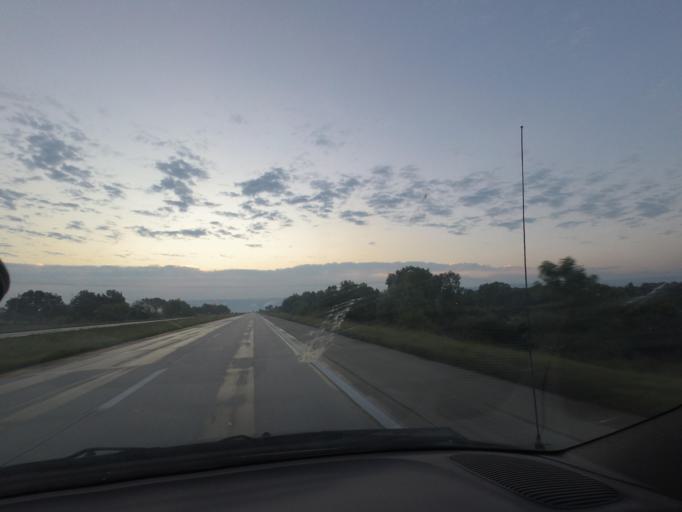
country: US
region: Missouri
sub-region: Macon County
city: Macon
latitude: 39.7606
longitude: -92.5761
